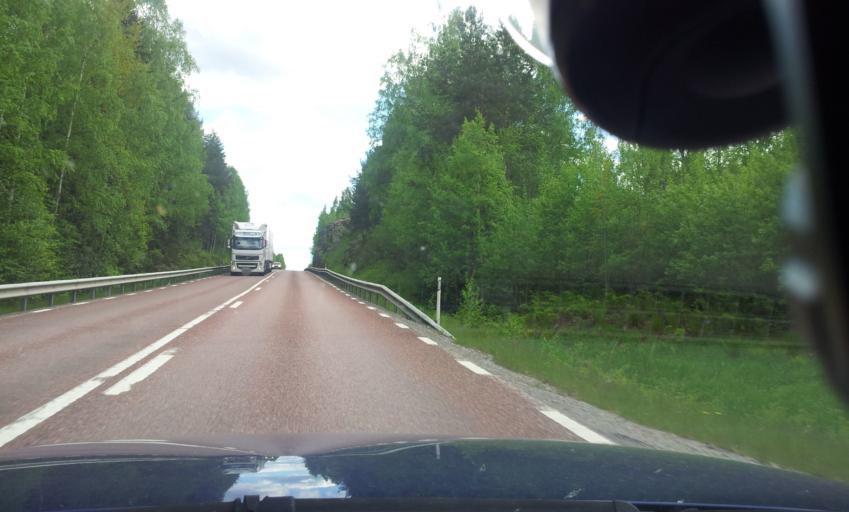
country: SE
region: Gaevleborg
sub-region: Bollnas Kommun
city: Arbra
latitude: 61.5505
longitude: 16.3499
